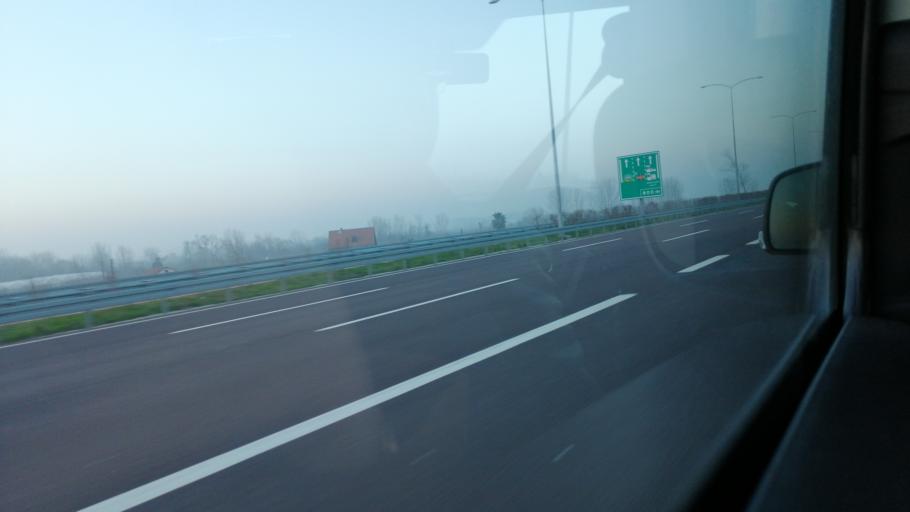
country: TR
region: Yalova
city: Altinova
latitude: 40.7017
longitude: 29.4904
